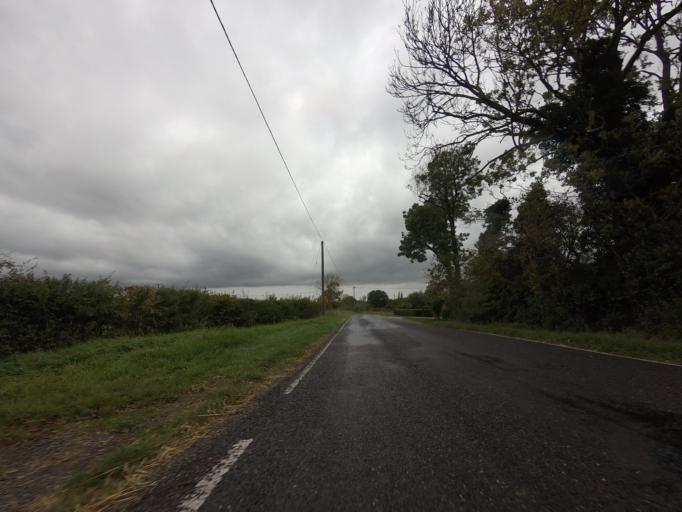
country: GB
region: England
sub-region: Cambridgeshire
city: Comberton
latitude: 52.1714
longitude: -0.0180
